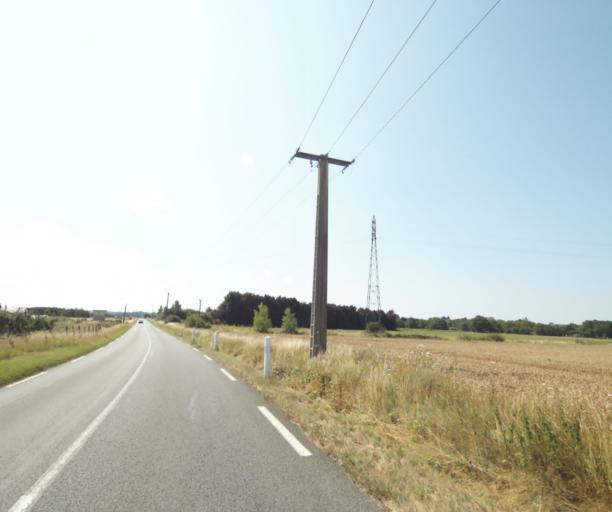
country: FR
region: Centre
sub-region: Departement du Loiret
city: Saint-Cyr-en-Val
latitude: 47.8450
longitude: 1.9580
